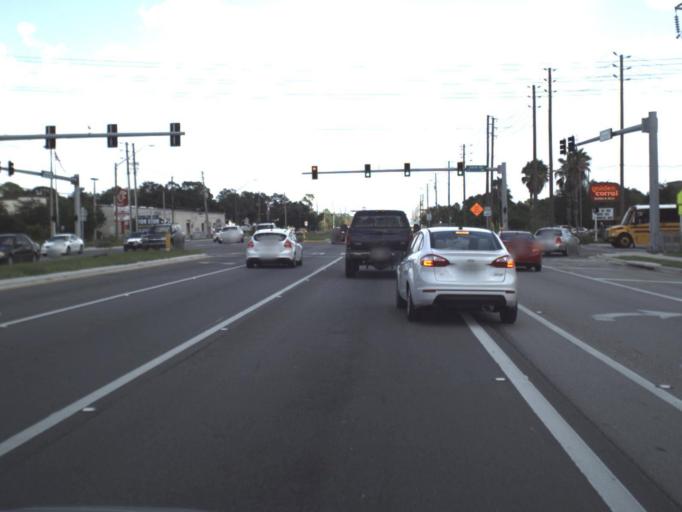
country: US
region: Florida
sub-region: Pinellas County
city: Largo
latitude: 27.8945
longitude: -82.7798
